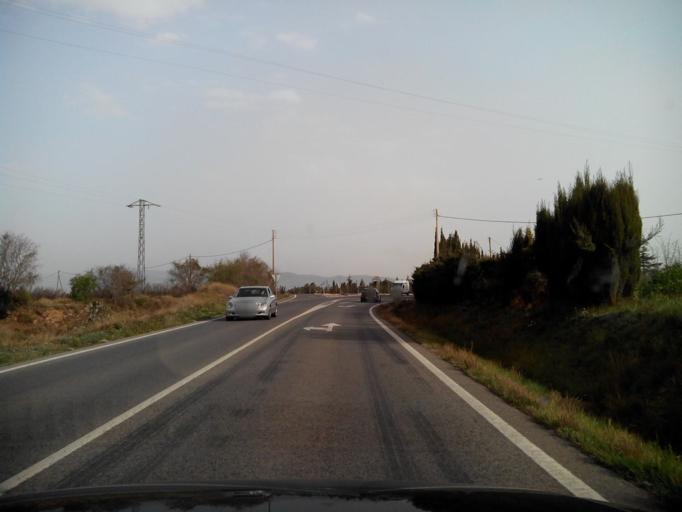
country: ES
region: Catalonia
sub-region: Provincia de Tarragona
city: Cambrils
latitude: 41.1041
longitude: 1.0838
